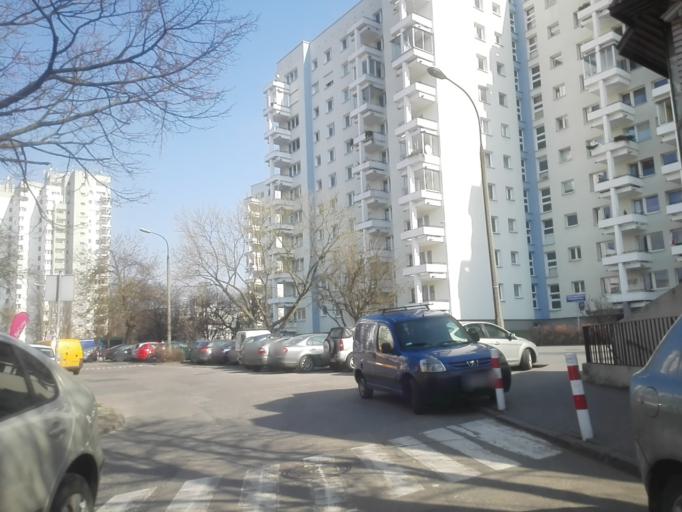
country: PL
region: Masovian Voivodeship
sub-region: Warszawa
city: Mokotow
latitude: 52.1720
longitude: 21.0207
